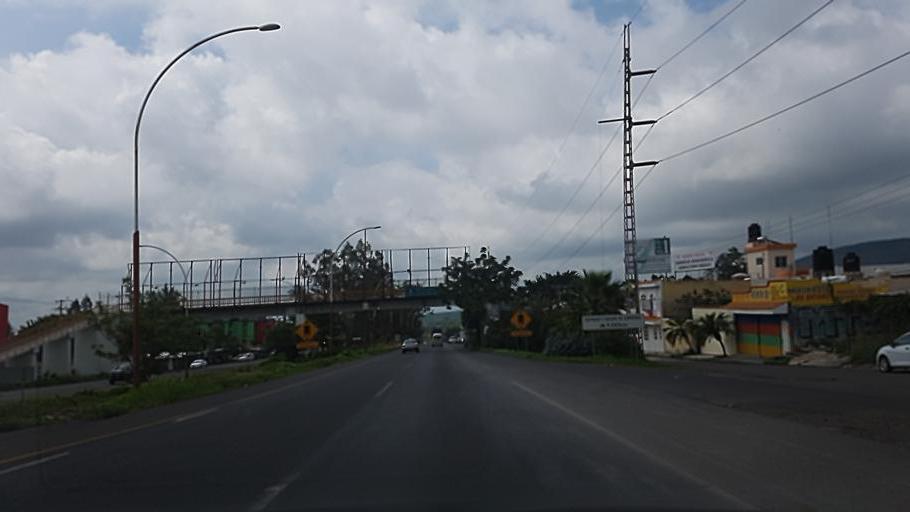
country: MX
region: Nayarit
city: Tepic
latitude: 21.5159
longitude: -104.9247
